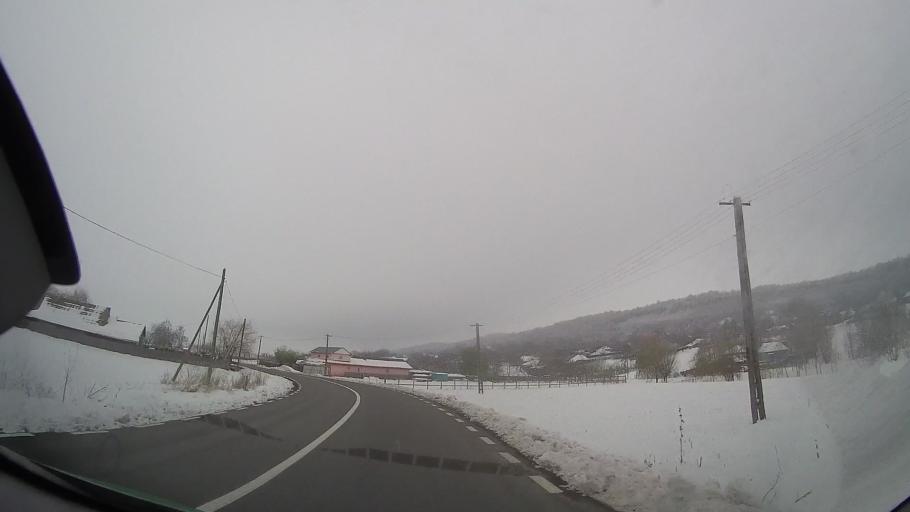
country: RO
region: Neamt
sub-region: Comuna Bozieni
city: Bozieni
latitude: 46.8533
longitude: 27.1771
